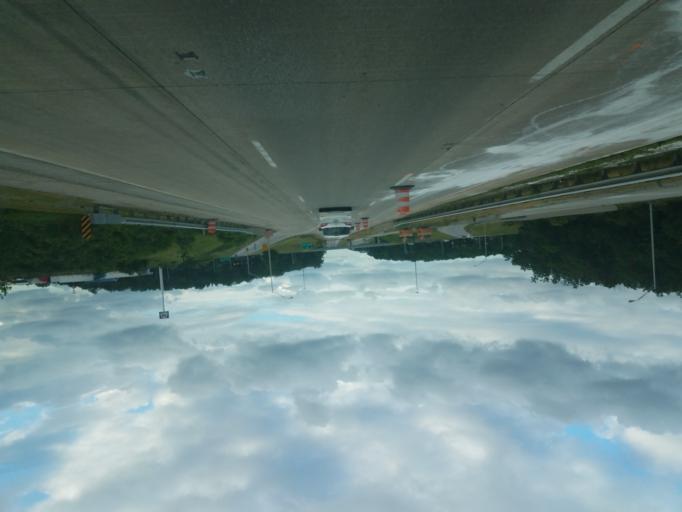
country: US
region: Indiana
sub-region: DeKalb County
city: Waterloo
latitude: 41.4433
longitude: -85.0538
